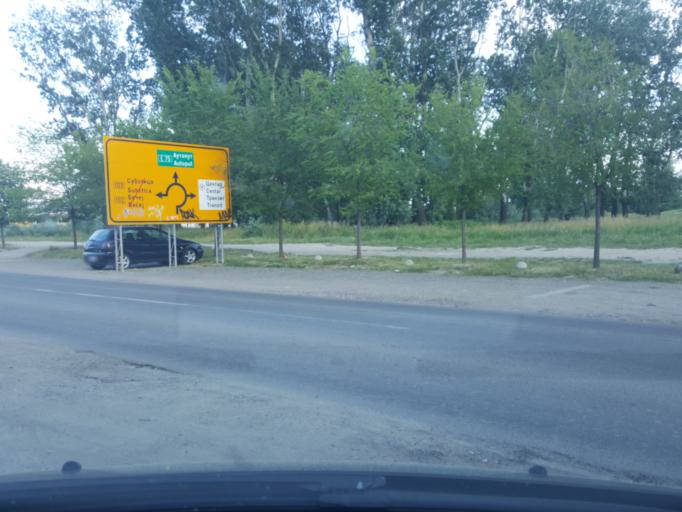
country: RS
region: Autonomna Pokrajina Vojvodina
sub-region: Juznobacki Okrug
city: Novi Sad
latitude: 45.2835
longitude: 19.8247
